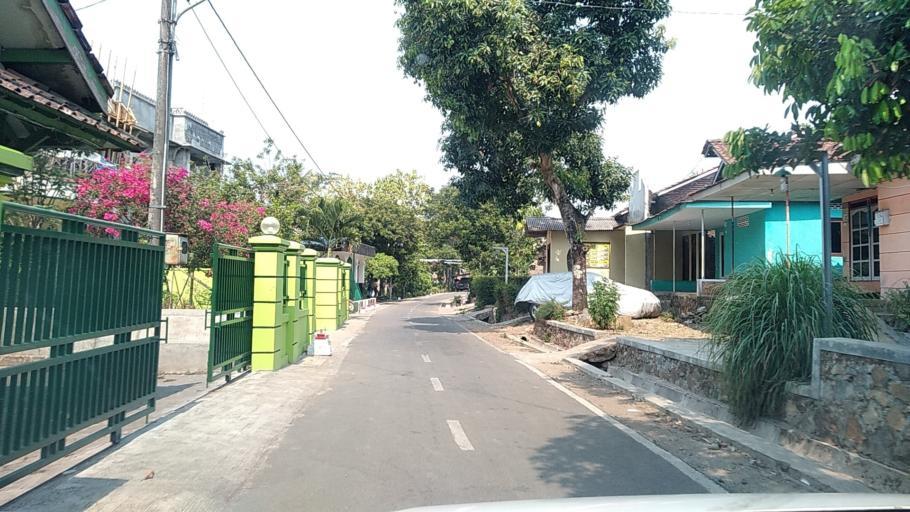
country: ID
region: Central Java
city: Ungaran
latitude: -7.0928
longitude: 110.3348
